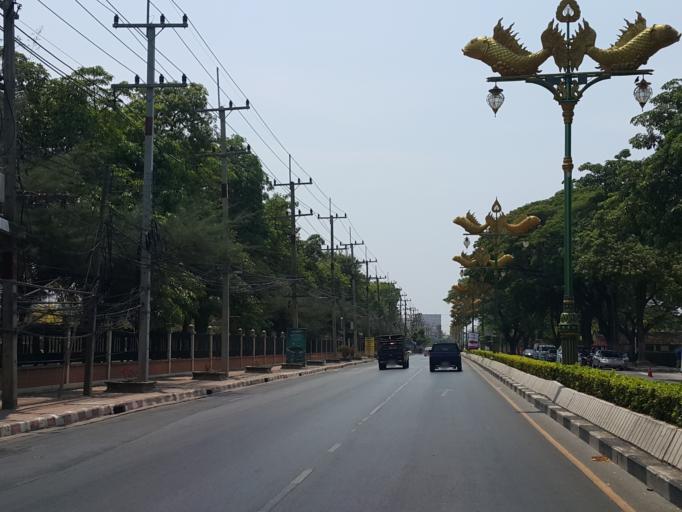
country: TH
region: Kanchanaburi
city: Kanchanaburi
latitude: 14.0325
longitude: 99.5253
